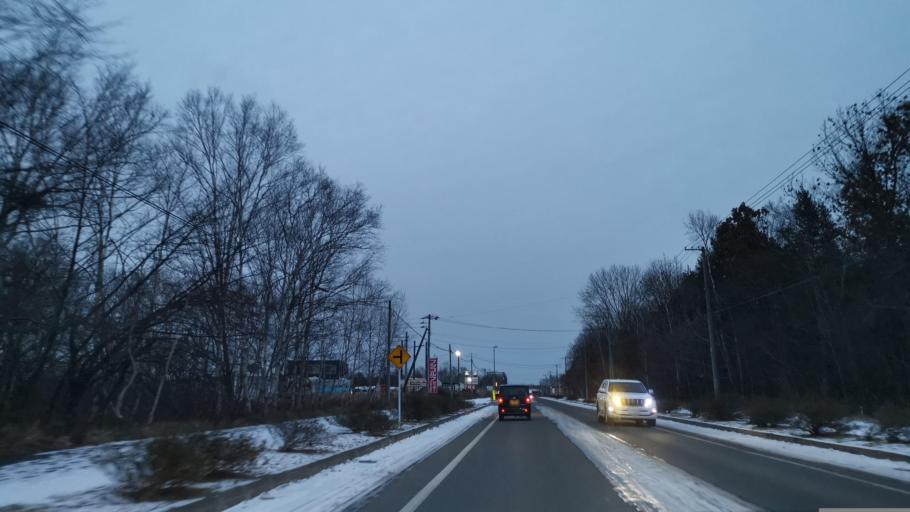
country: JP
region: Hokkaido
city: Chitose
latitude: 42.8163
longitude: 141.6718
